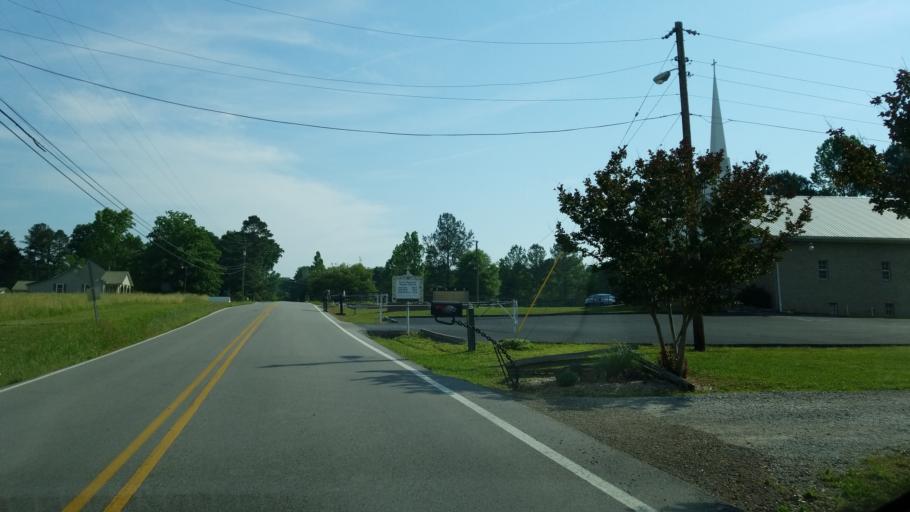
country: US
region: Tennessee
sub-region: Hamilton County
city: Collegedale
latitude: 35.0623
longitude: -85.0121
